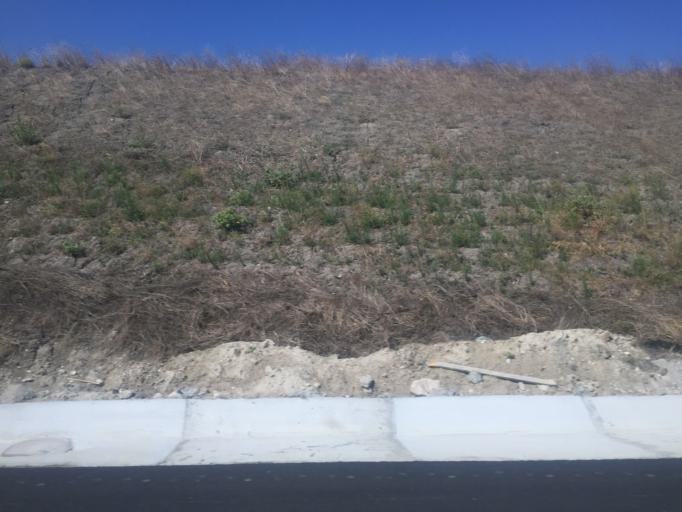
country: TR
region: Balikesir
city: Susurluk
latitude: 39.9636
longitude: 28.1643
